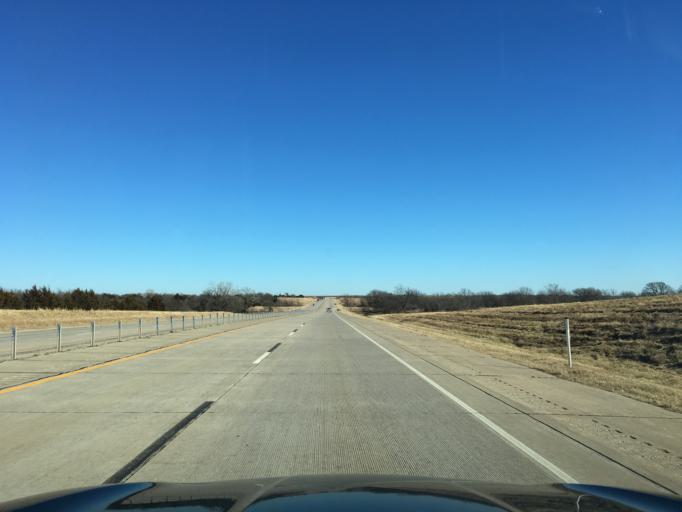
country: US
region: Oklahoma
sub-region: Payne County
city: Yale
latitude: 36.2249
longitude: -96.7097
